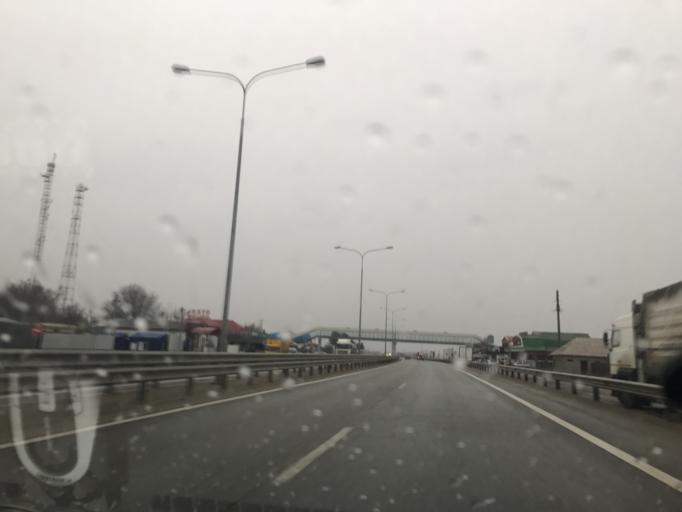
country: RU
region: Krasnodarskiy
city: Krylovskaya
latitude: 46.2839
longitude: 39.8293
